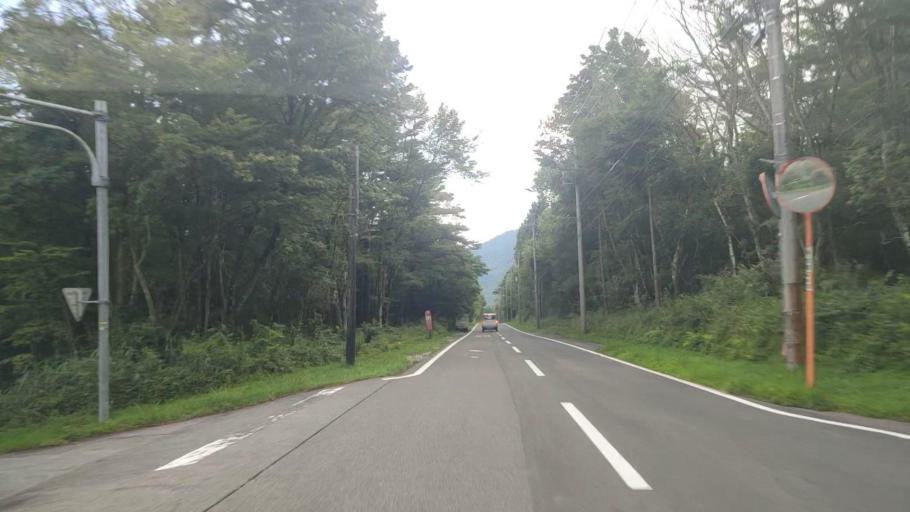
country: JP
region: Shizuoka
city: Gotemba
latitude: 35.2679
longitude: 138.8035
